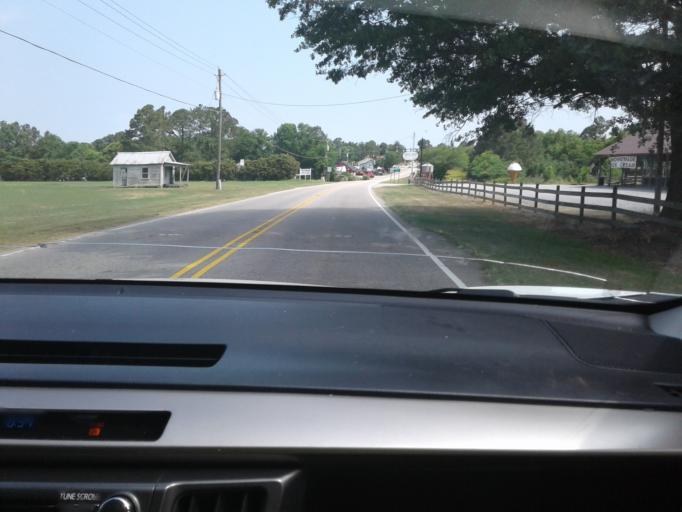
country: US
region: North Carolina
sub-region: Harnett County
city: Coats
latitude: 35.3984
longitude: -78.6726
